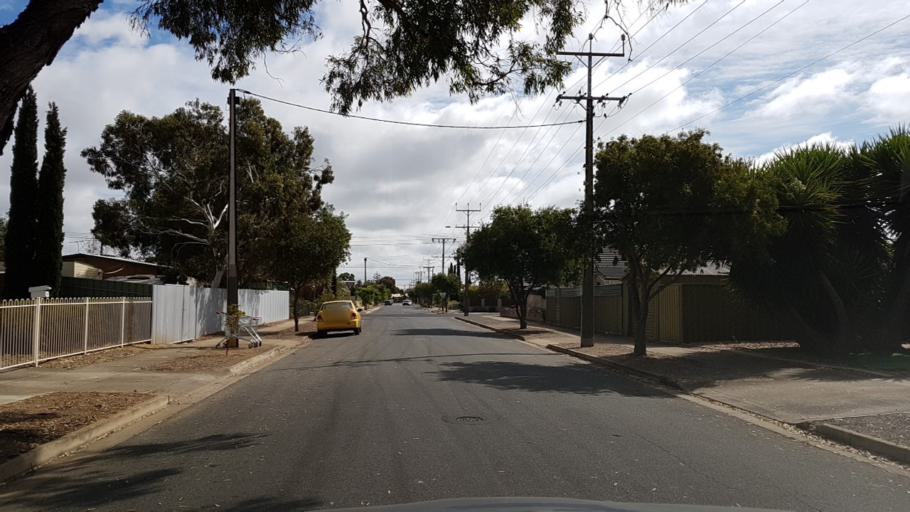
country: AU
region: South Australia
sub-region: Marion
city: Plympton Park
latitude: -34.9862
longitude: 138.5500
